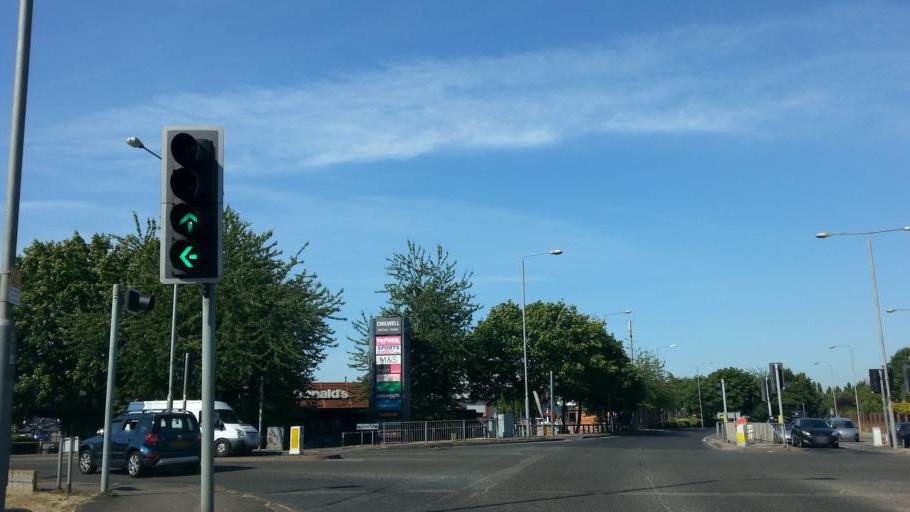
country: GB
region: England
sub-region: Derbyshire
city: Long Eaton
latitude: 52.9042
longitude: -1.2433
